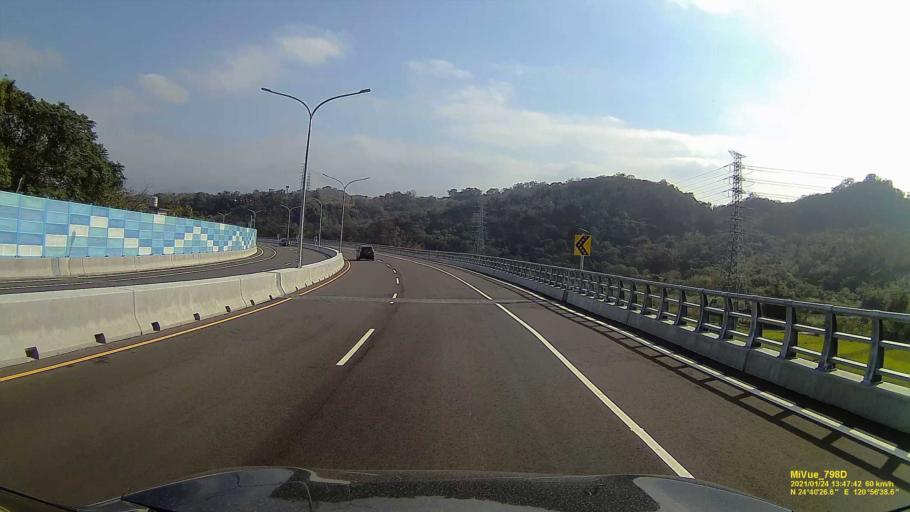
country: TW
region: Taiwan
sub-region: Hsinchu
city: Hsinchu
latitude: 24.6738
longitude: 120.9443
